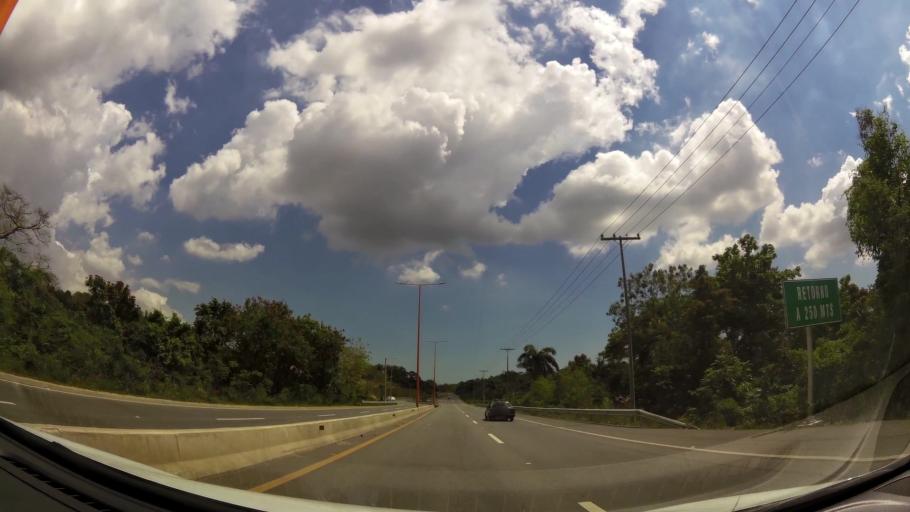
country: DO
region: Nacional
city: Santo Domingo
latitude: 18.5492
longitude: -69.9675
